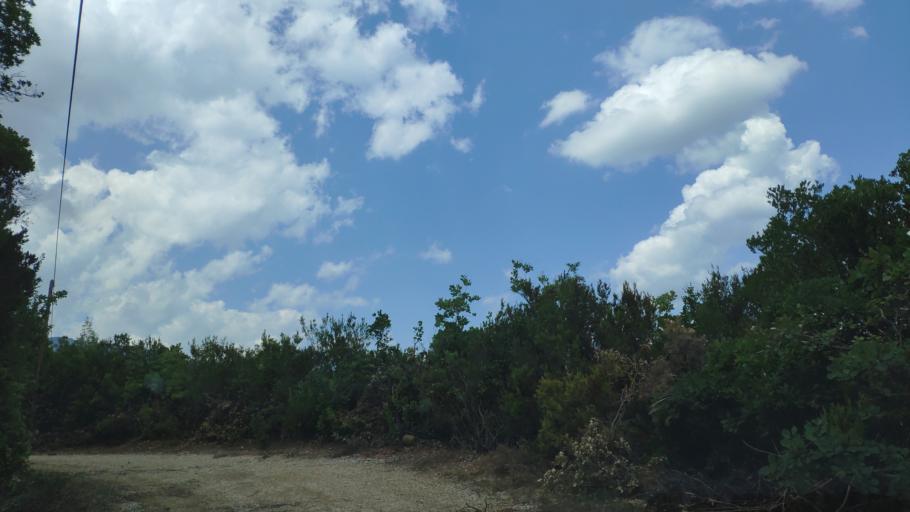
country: GR
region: Epirus
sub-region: Nomos Artas
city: Agios Dimitrios
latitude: 39.3148
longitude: 21.0176
